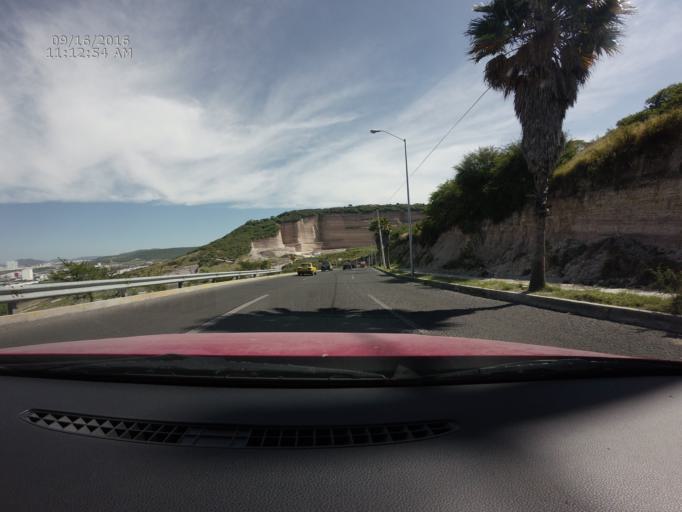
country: MX
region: Queretaro
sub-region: Queretaro
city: Sergio Villasenor
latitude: 20.6466
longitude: -100.4252
